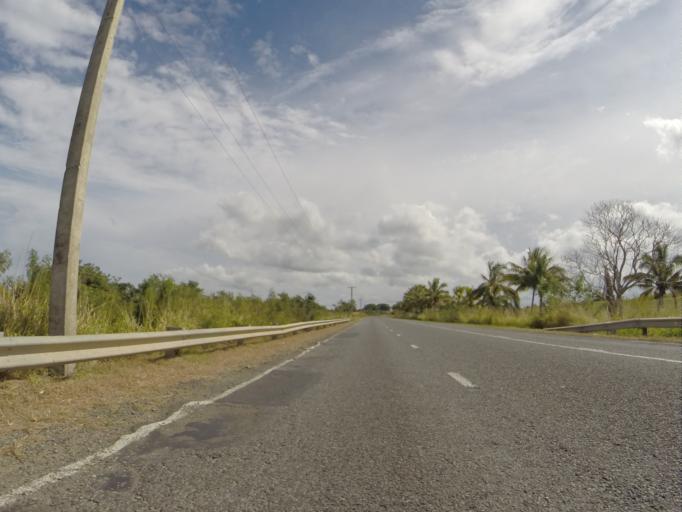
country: FJ
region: Western
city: Nadi
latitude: -18.1141
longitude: 177.4077
